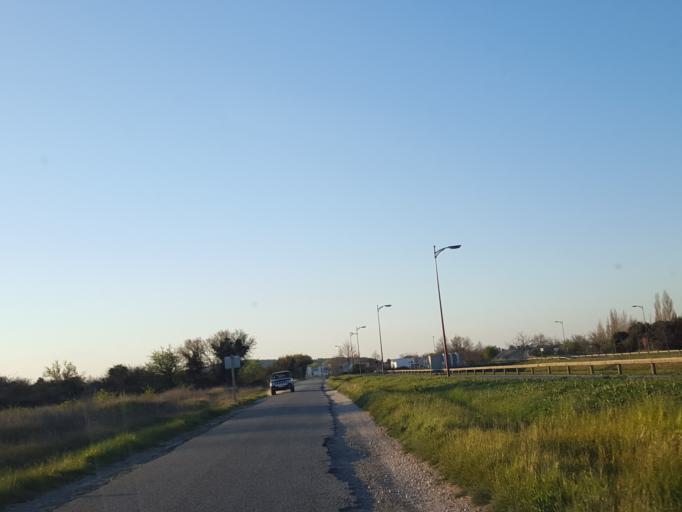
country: FR
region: Provence-Alpes-Cote d'Azur
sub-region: Departement du Vaucluse
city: Entraigues-sur-la-Sorgue
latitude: 43.9895
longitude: 4.9257
